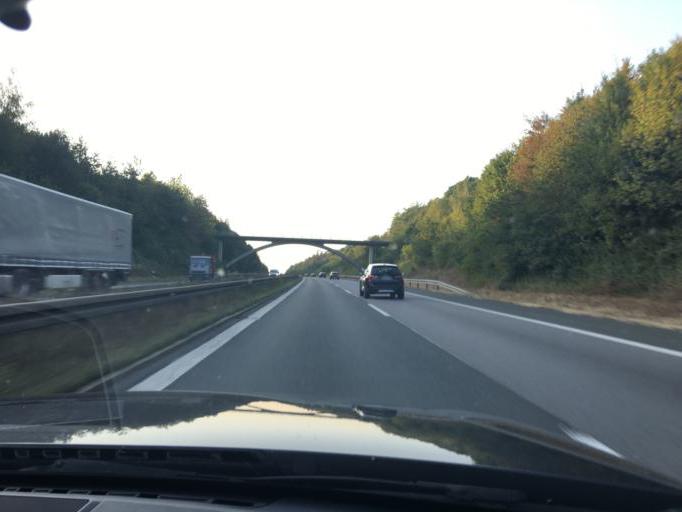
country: DE
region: Bavaria
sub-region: Upper Franconia
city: Strullendorf
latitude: 49.8465
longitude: 10.9948
